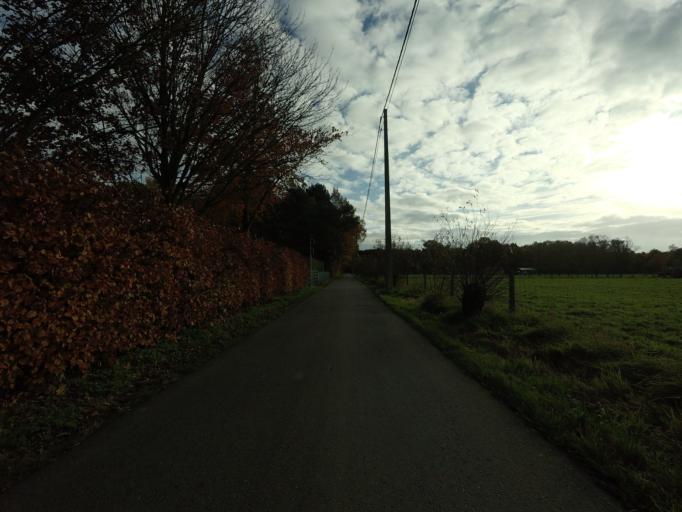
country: BE
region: Flanders
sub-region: Provincie Antwerpen
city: Bonheiden
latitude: 51.0353
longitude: 4.5776
